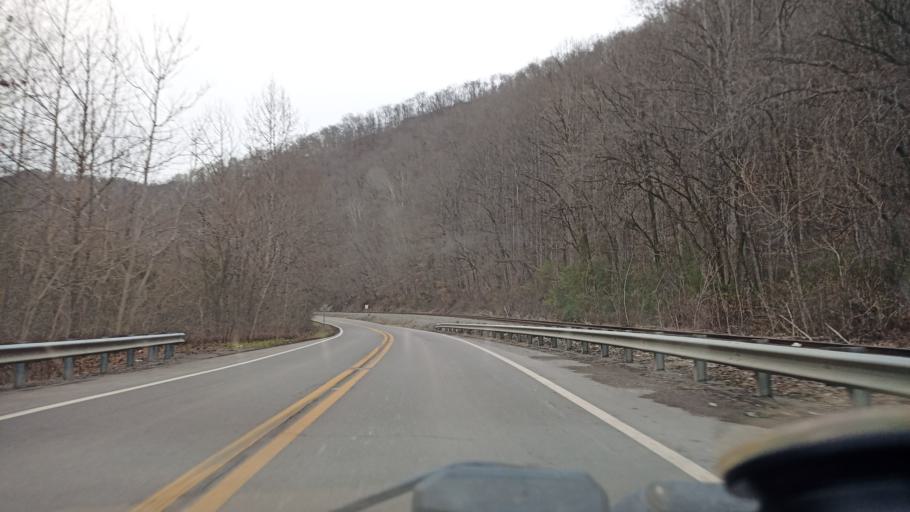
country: US
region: West Virginia
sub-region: Logan County
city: Mallory
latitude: 37.6922
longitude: -81.8566
